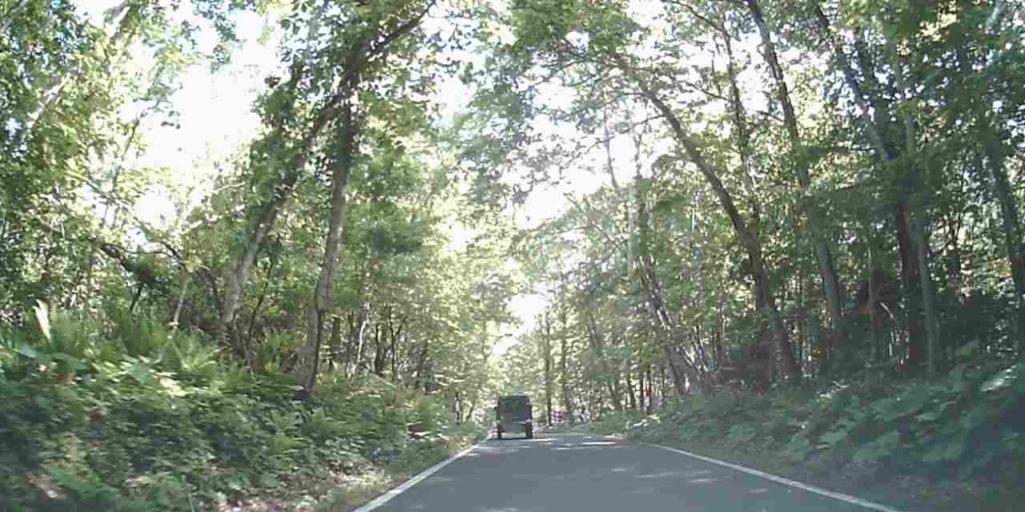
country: JP
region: Hokkaido
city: Shiraoi
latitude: 42.7364
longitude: 141.4108
